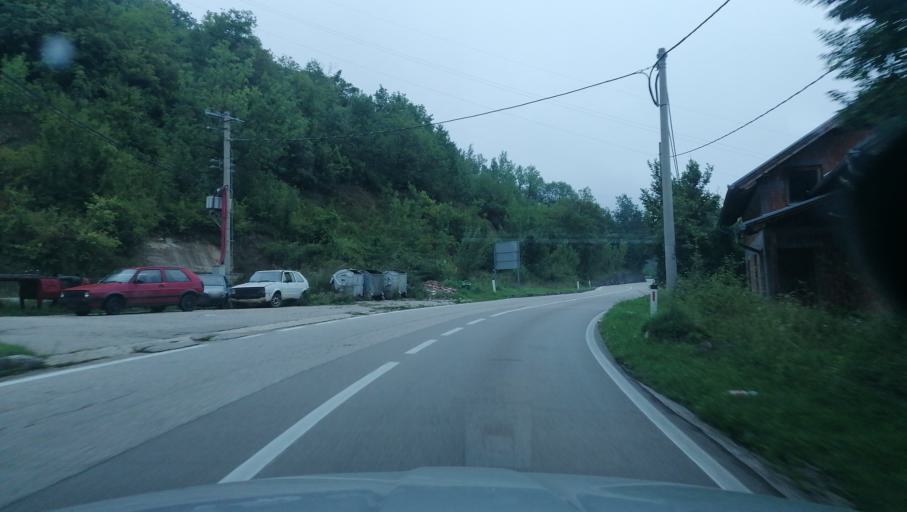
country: BA
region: Federation of Bosnia and Herzegovina
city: Jablanica
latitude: 43.7027
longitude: 17.7161
